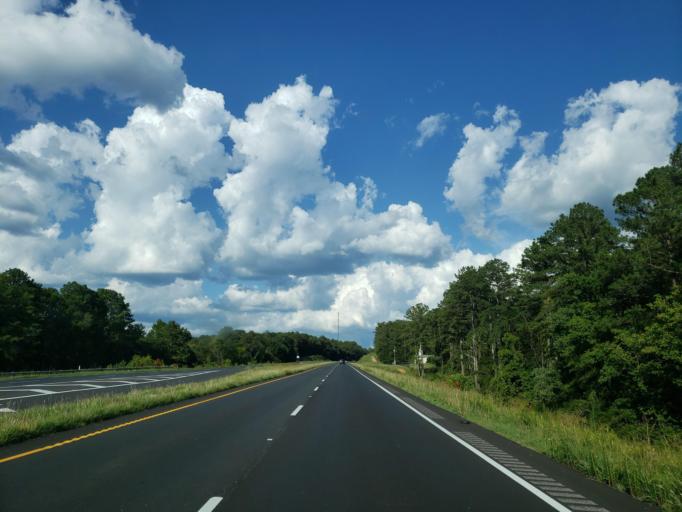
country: US
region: Georgia
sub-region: Floyd County
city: Rome
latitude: 34.2078
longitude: -85.0578
